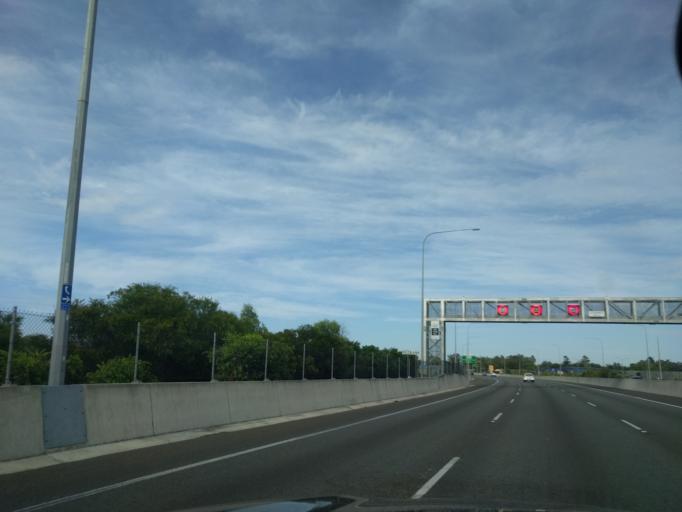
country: AU
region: Queensland
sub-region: Ipswich
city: Redbank
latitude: -27.6012
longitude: 152.8775
